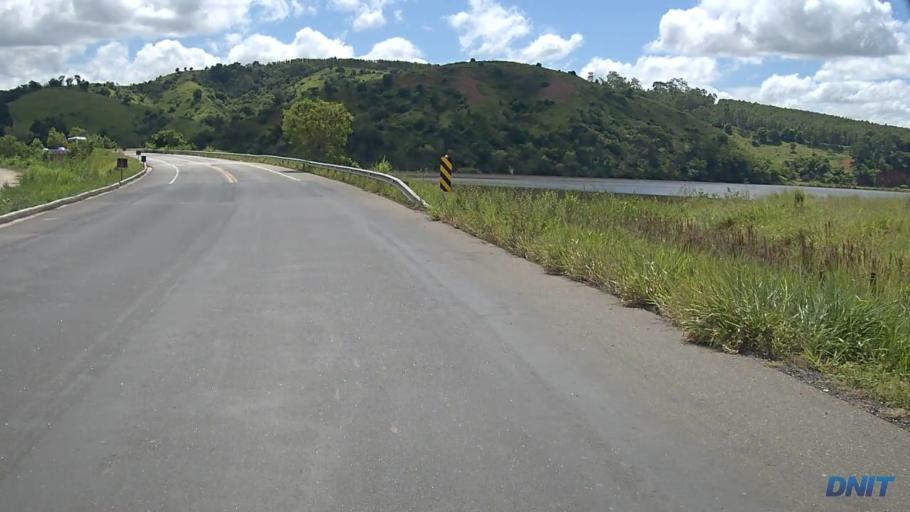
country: BR
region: Minas Gerais
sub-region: Governador Valadares
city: Governador Valadares
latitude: -19.0440
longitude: -42.1516
